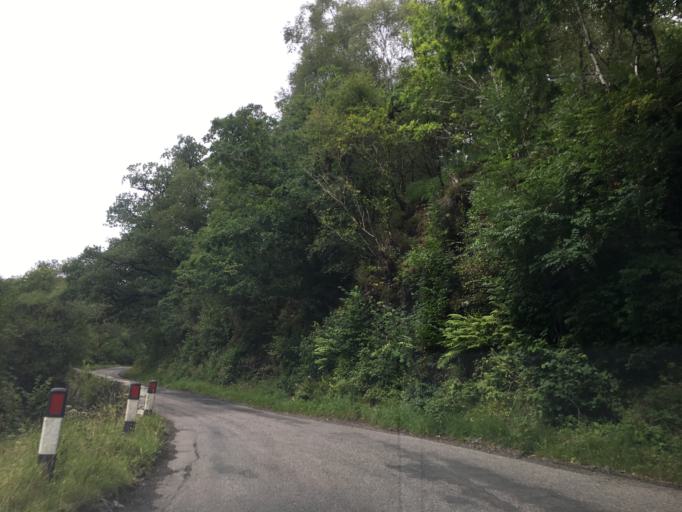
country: GB
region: Scotland
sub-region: Argyll and Bute
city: Oban
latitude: 56.4013
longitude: -5.2153
